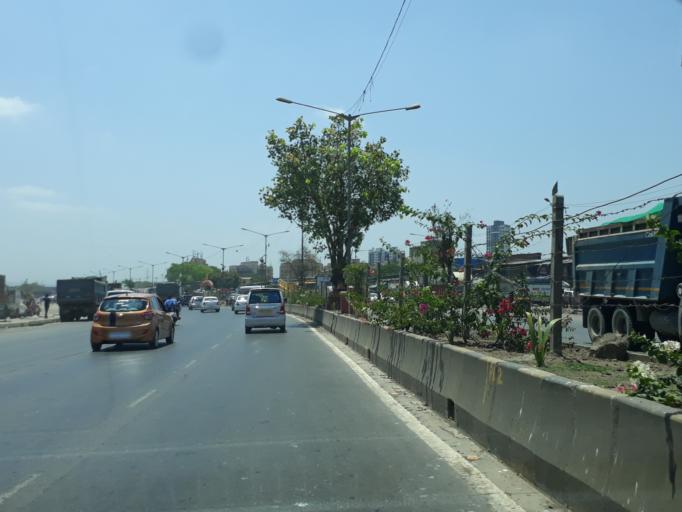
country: IN
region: Maharashtra
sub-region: Mumbai Suburban
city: Mumbai
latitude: 19.0570
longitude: 72.9281
